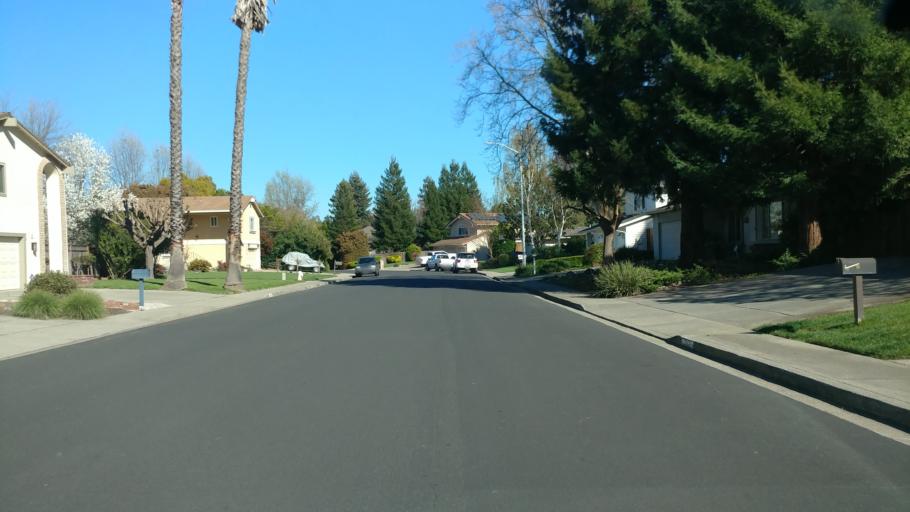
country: US
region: California
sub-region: Contra Costa County
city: San Ramon
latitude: 37.7850
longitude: -121.9735
